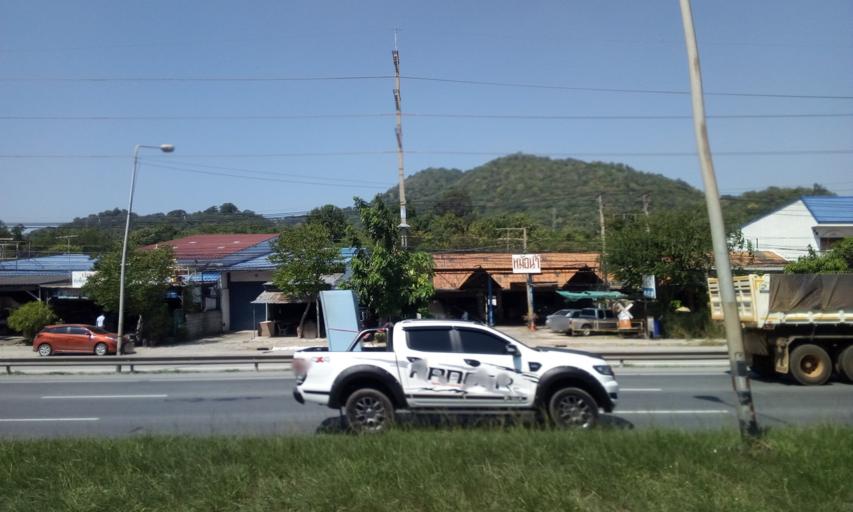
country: TH
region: Sara Buri
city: Muak Lek
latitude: 14.6286
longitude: 101.1786
